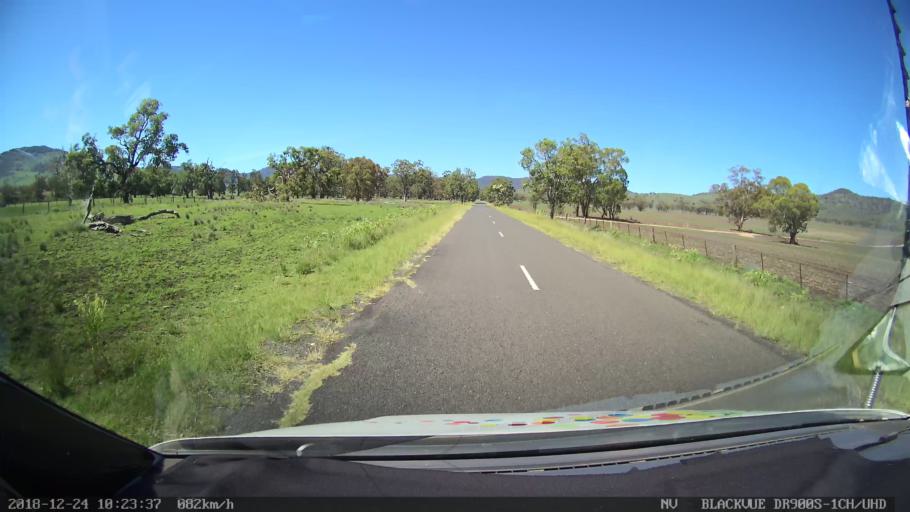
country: AU
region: New South Wales
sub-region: Liverpool Plains
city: Quirindi
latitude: -31.7772
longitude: 150.5367
